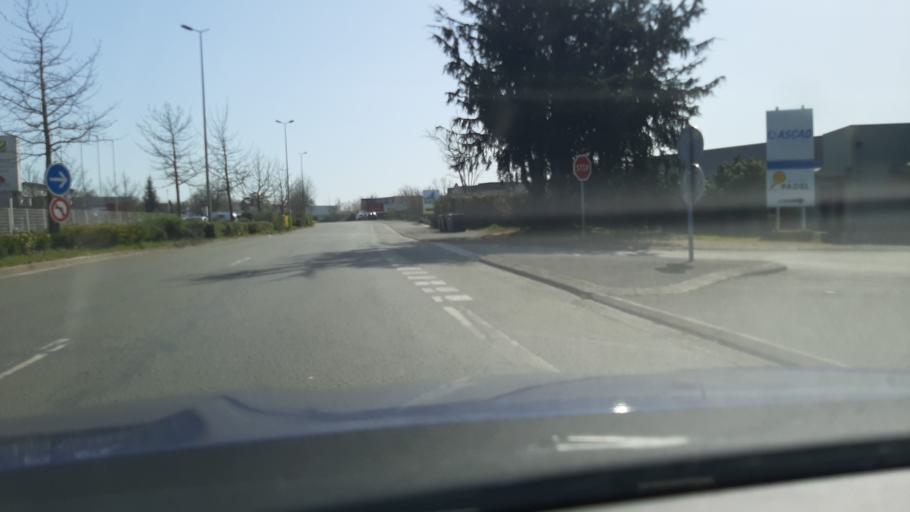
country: FR
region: Pays de la Loire
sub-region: Departement de Maine-et-Loire
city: Angers
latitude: 47.4837
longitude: -0.5061
